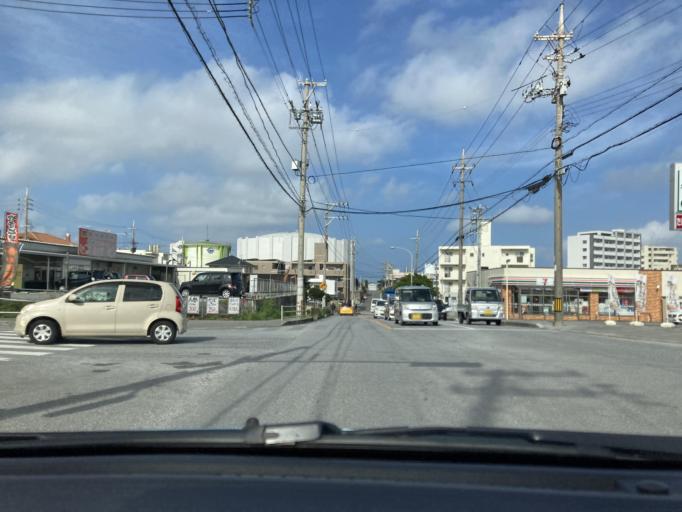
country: JP
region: Okinawa
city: Ginowan
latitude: 26.2558
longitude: 127.7706
